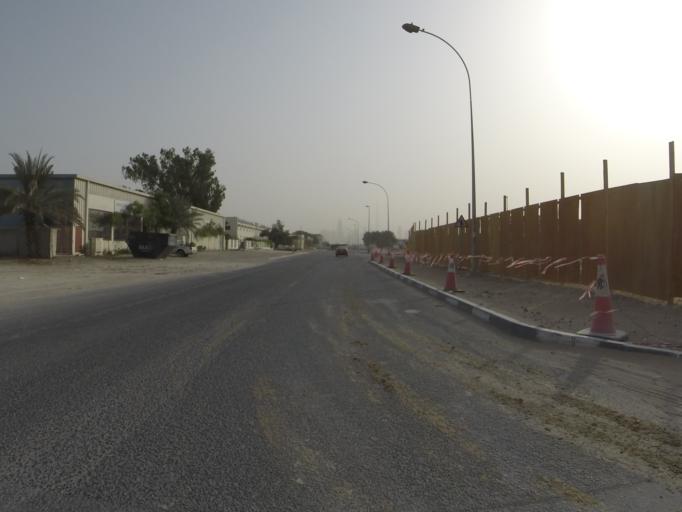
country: AE
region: Dubai
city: Dubai
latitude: 25.1496
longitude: 55.2293
